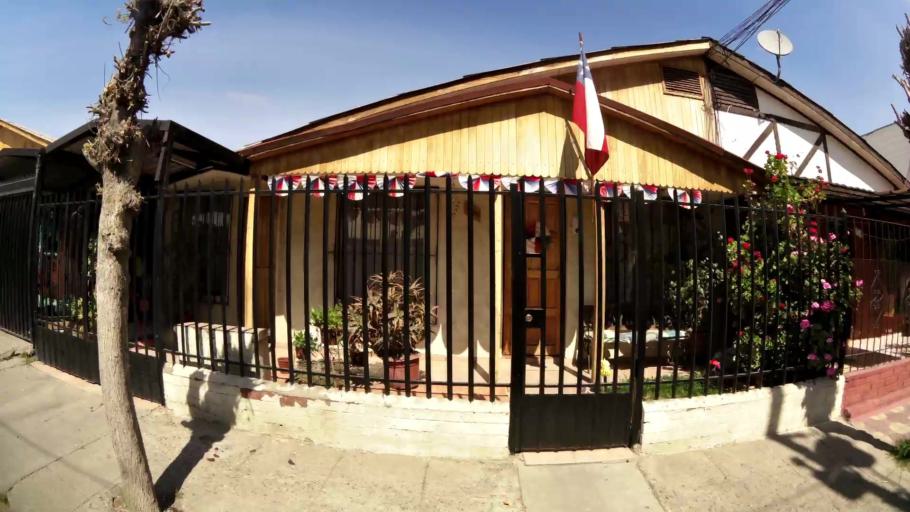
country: CL
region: Santiago Metropolitan
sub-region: Provincia de Cordillera
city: Puente Alto
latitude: -33.5729
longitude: -70.5730
